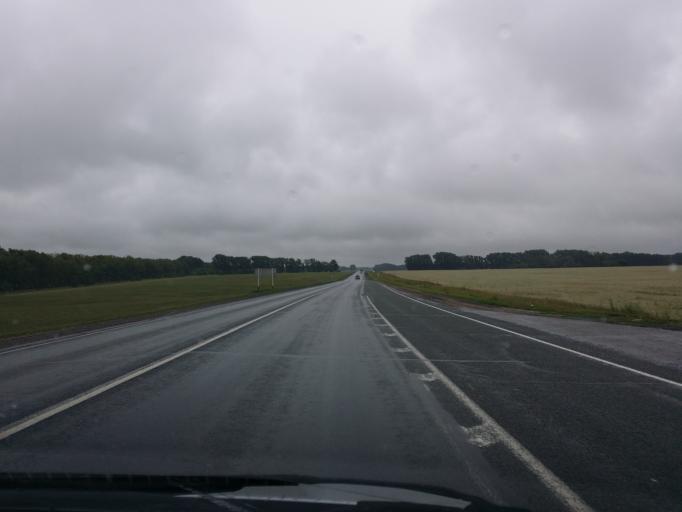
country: RU
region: Altai Krai
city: Bayunovskiye Klyuchi
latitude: 53.2888
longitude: 84.3240
